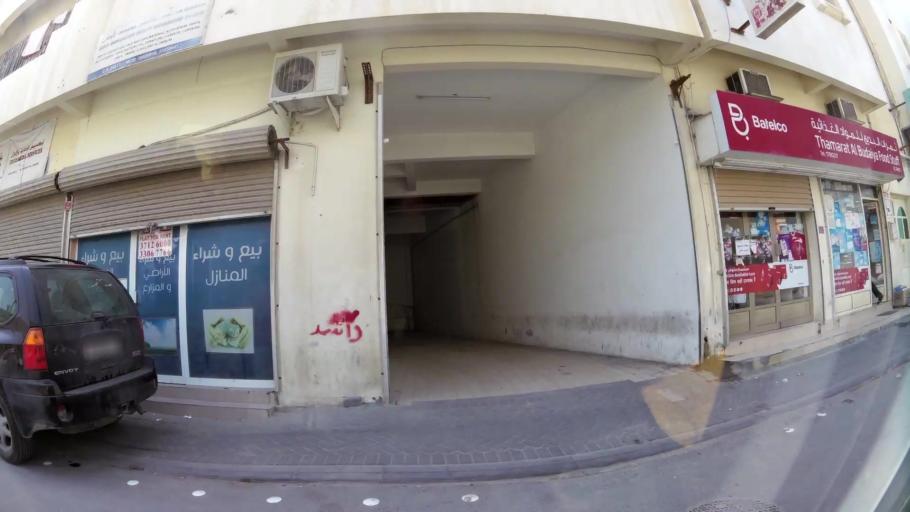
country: BH
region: Manama
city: Jidd Hafs
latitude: 26.2171
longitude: 50.4503
